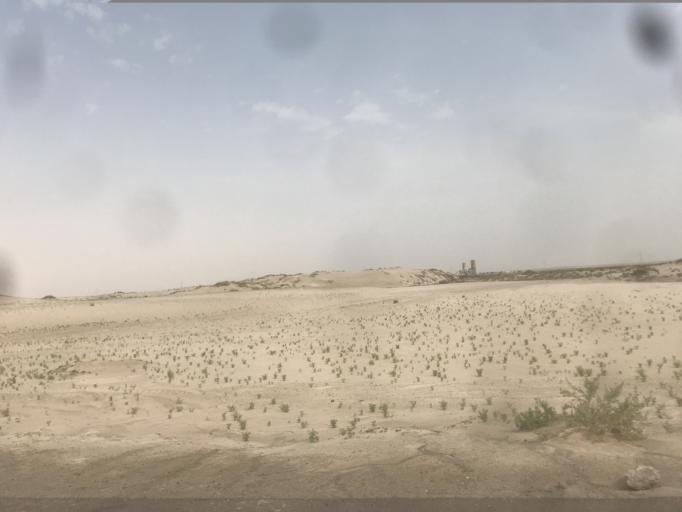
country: SA
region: Eastern Province
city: Abqaiq
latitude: 25.9057
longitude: 50.0124
